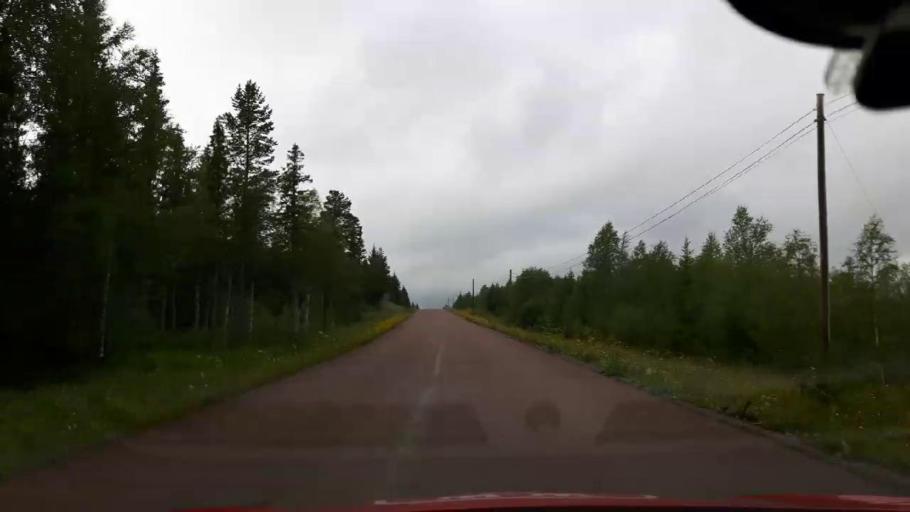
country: SE
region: Jaemtland
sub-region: Krokoms Kommun
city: Valla
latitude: 63.3899
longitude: 13.8333
